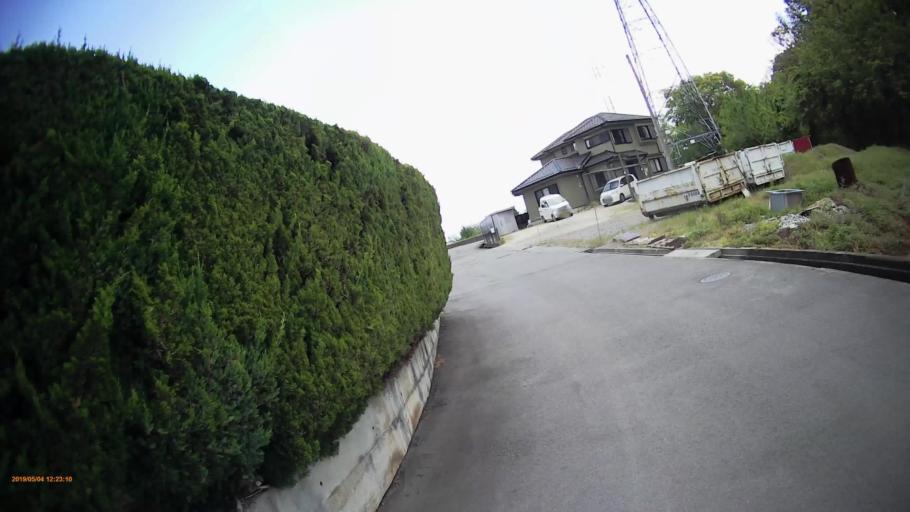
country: JP
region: Yamanashi
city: Ryuo
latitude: 35.6782
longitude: 138.5043
